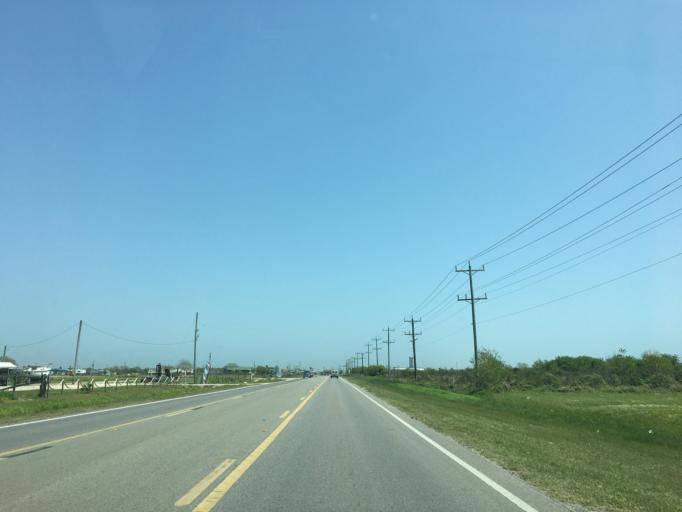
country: US
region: Texas
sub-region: Galveston County
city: Bolivar Peninsula
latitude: 29.4527
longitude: -94.6484
